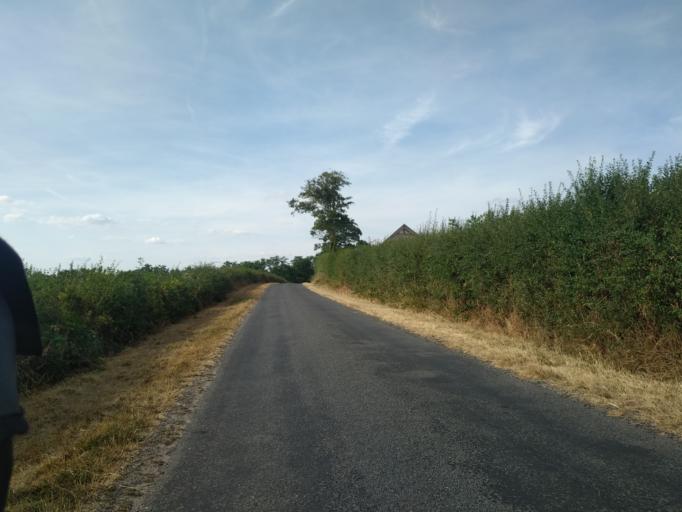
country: FR
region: Bourgogne
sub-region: Departement de Saone-et-Loire
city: Bourbon-Lancy
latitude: 46.6729
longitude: 3.7598
